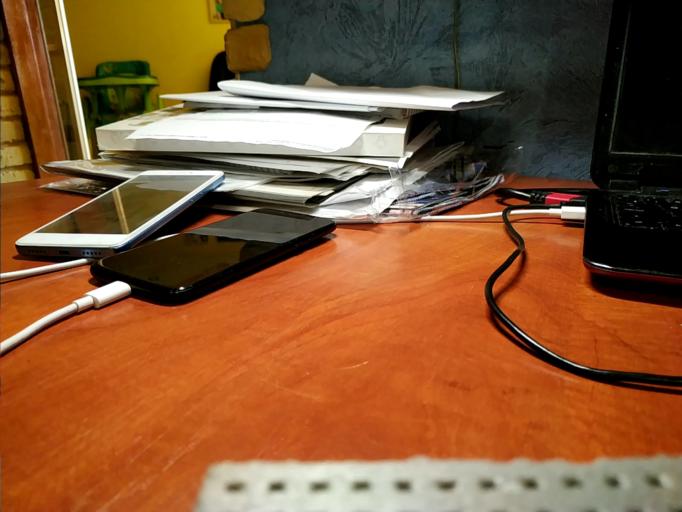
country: RU
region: Tverskaya
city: Kalashnikovo
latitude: 57.4063
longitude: 35.1947
